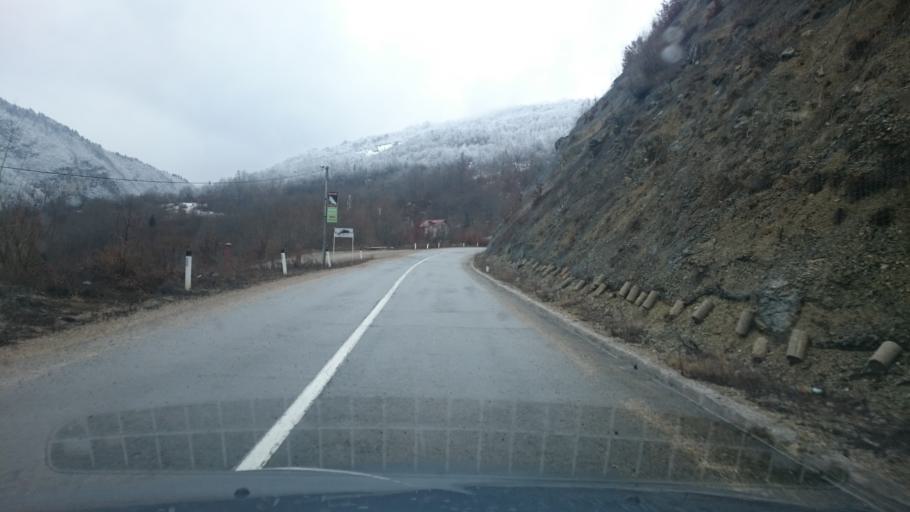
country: BA
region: Republika Srpska
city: Skender Vakuf
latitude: 44.4398
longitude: 17.3960
